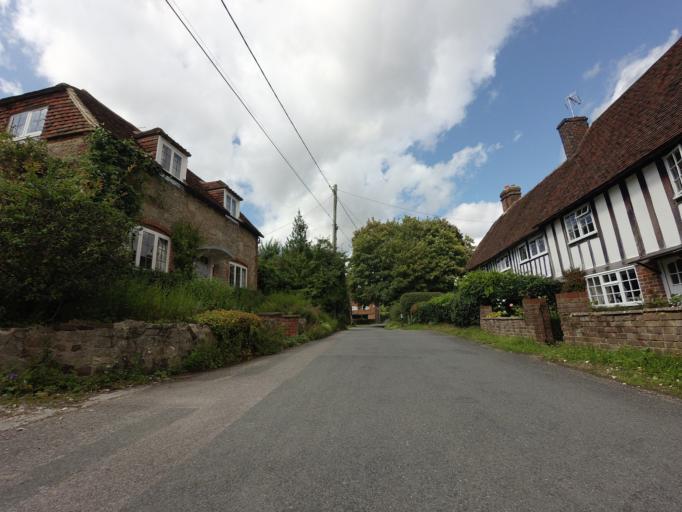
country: GB
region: England
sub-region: Kent
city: Borough Green
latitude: 51.2622
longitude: 0.2951
